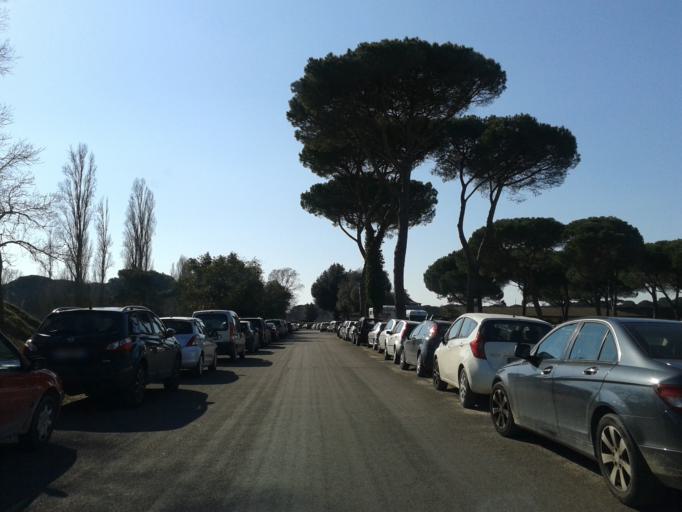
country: IT
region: Tuscany
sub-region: Province of Pisa
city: Madonna dell'Acqua
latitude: 43.7253
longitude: 10.3391
